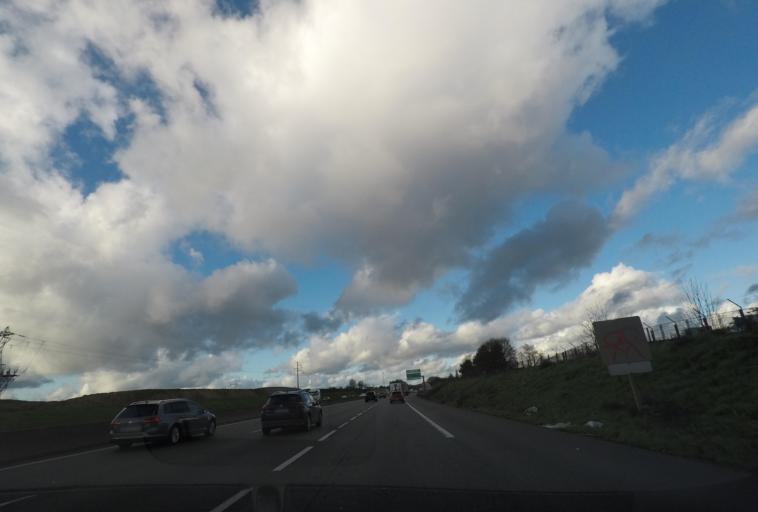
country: FR
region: Ile-de-France
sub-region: Departement de l'Essonne
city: Ormoy
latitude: 48.5676
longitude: 2.4725
